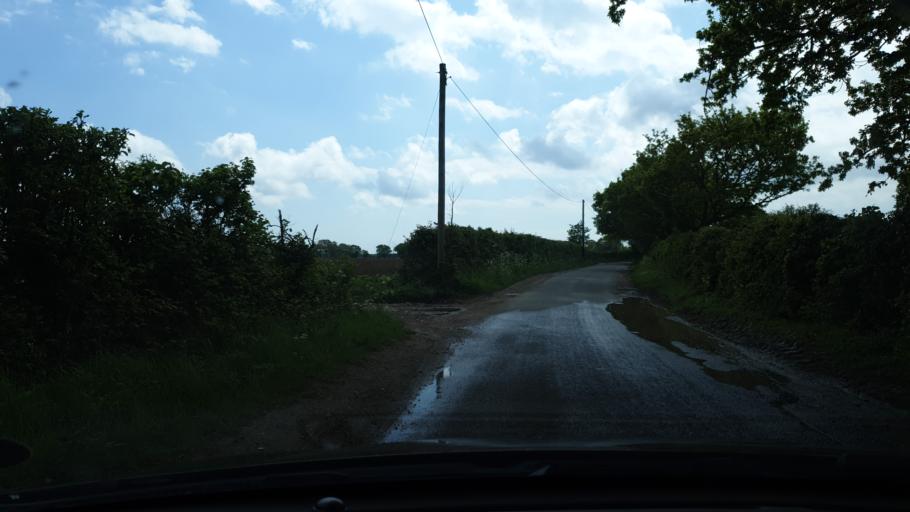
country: GB
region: England
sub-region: Essex
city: Great Bentley
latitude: 51.8763
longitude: 1.0603
